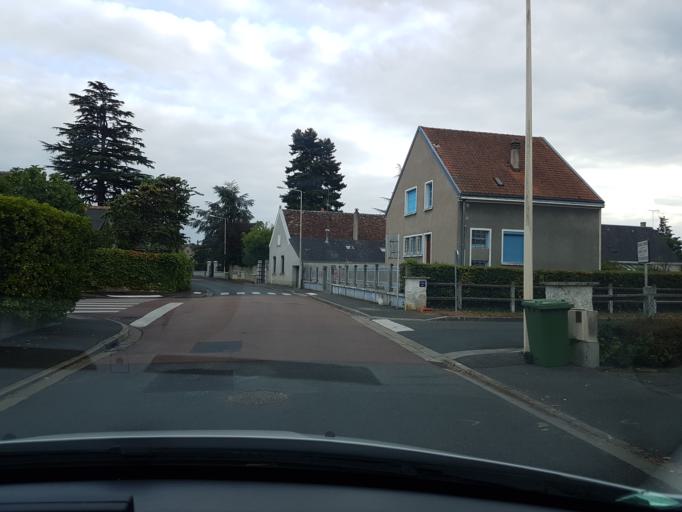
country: FR
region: Centre
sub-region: Departement d'Indre-et-Loire
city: Saint-Avertin
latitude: 47.3647
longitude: 0.7386
